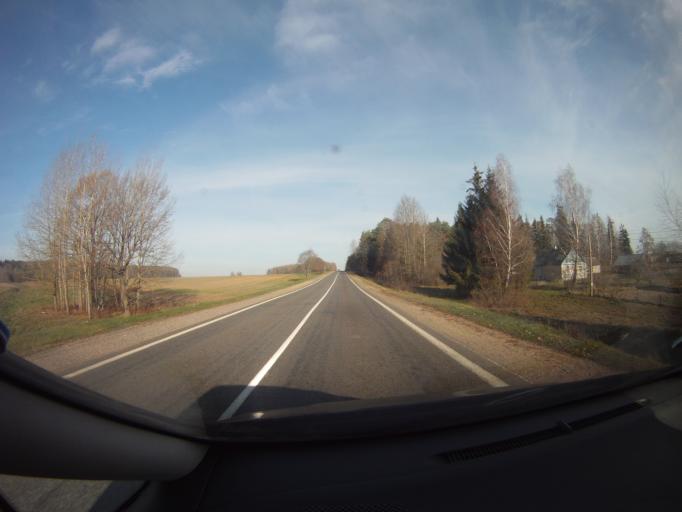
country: BY
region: Minsk
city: Il'ya
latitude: 54.4541
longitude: 27.2838
